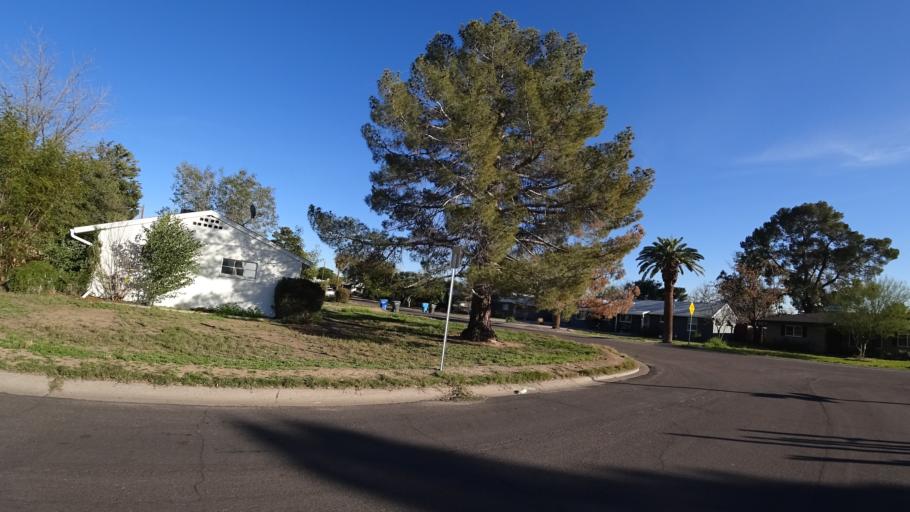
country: US
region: Arizona
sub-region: Maricopa County
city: Phoenix
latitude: 33.5230
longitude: -112.0461
